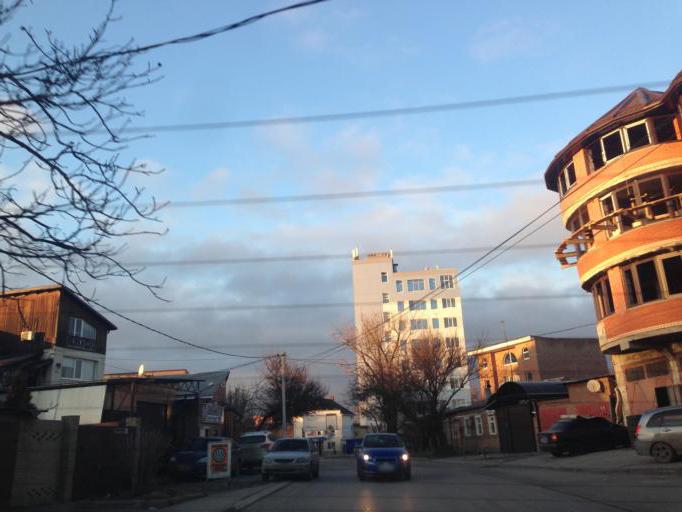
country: RU
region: Rostov
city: Rostov-na-Donu
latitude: 47.2482
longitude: 39.6797
